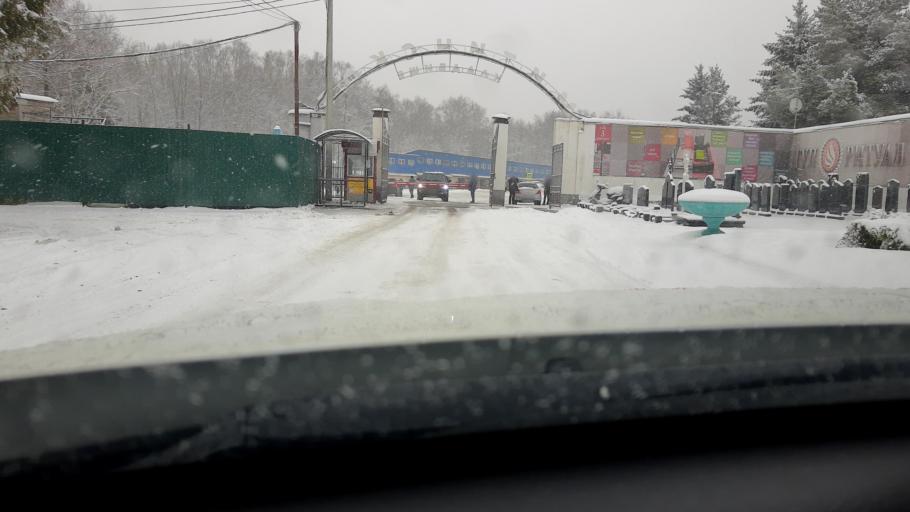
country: RU
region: Moskovskaya
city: Krasnogorsk
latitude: 55.8718
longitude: 37.3475
